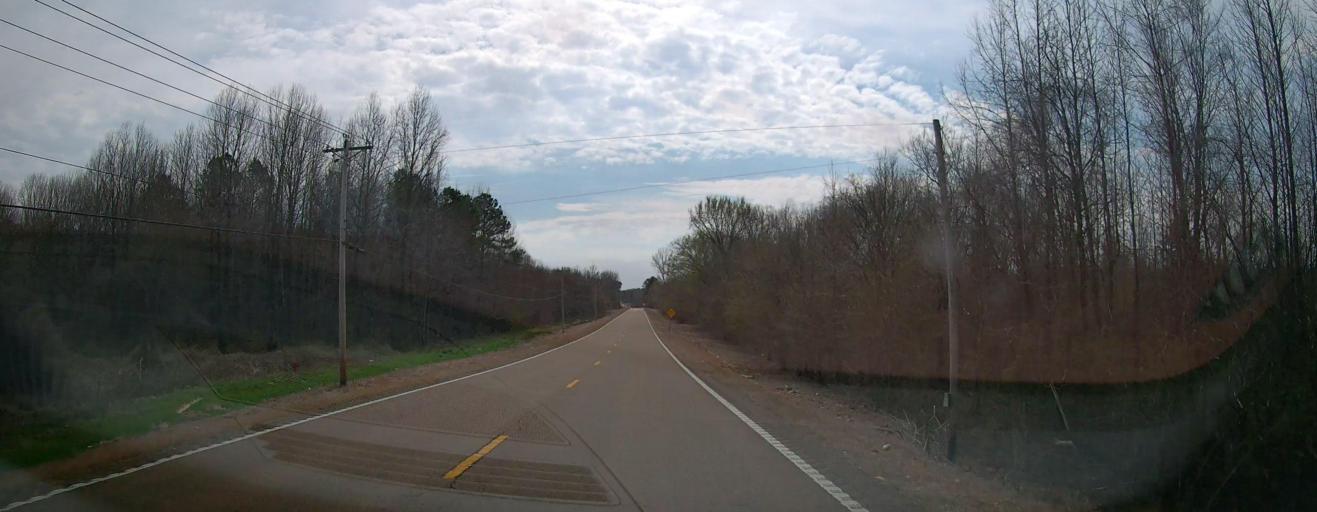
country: US
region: Mississippi
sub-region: Marshall County
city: Holly Springs
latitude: 34.7325
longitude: -89.4208
